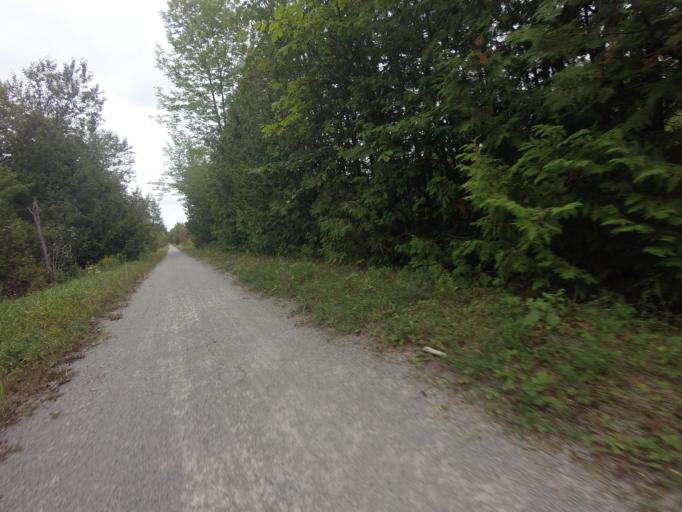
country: CA
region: Ontario
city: Uxbridge
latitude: 44.2970
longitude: -78.9533
